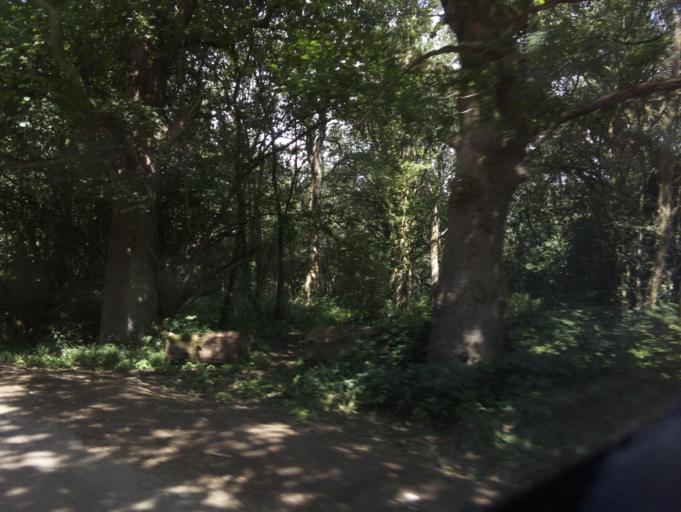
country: GB
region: England
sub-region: Wiltshire
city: Hankerton
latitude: 51.6218
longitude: -2.0129
